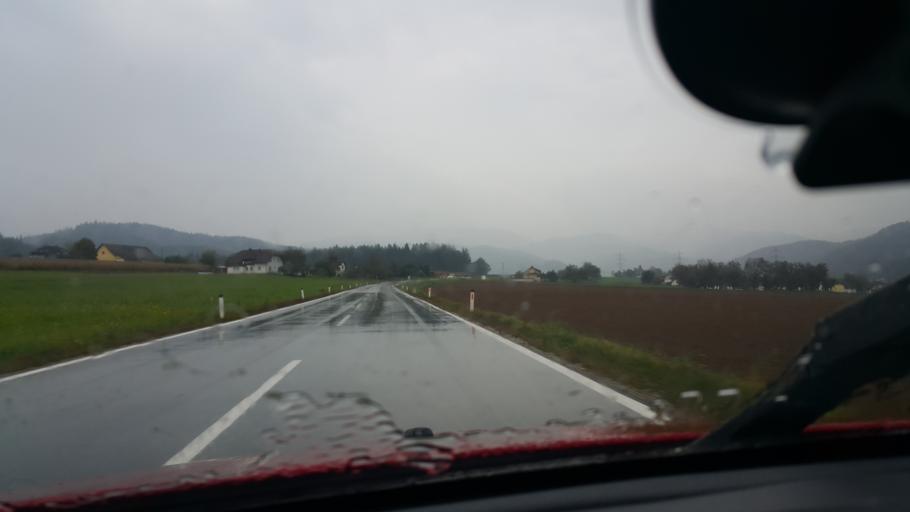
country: AT
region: Carinthia
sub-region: Politischer Bezirk Volkermarkt
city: Ruden
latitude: 46.6798
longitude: 14.7591
